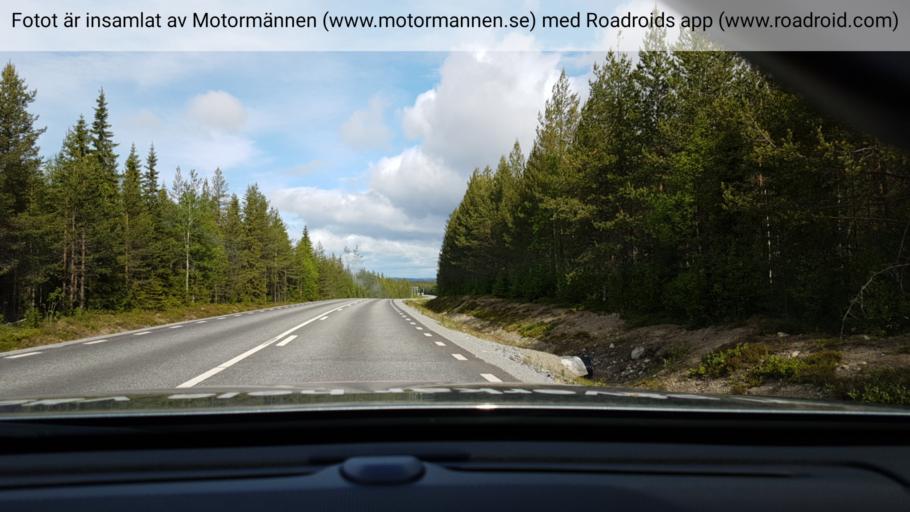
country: SE
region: Vaesterbotten
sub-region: Lycksele Kommun
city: Lycksele
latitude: 64.0737
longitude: 18.3528
